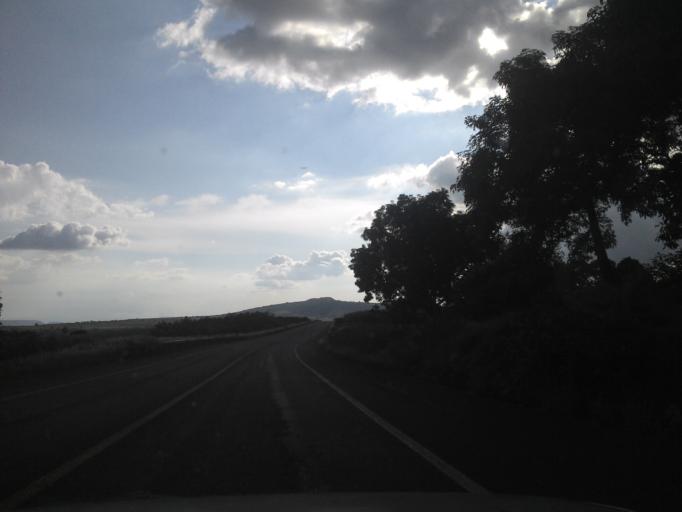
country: MX
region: Jalisco
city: Atotonilco el Alto
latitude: 20.5788
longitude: -102.5037
